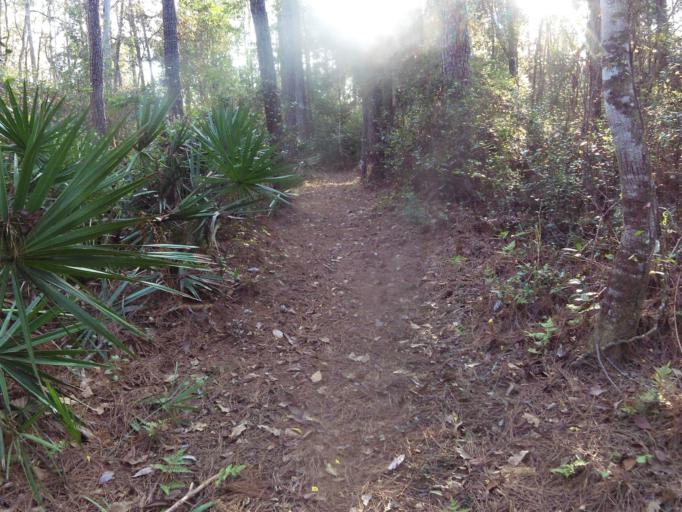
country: US
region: Florida
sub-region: Putnam County
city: Interlachen
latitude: 29.7676
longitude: -81.8383
